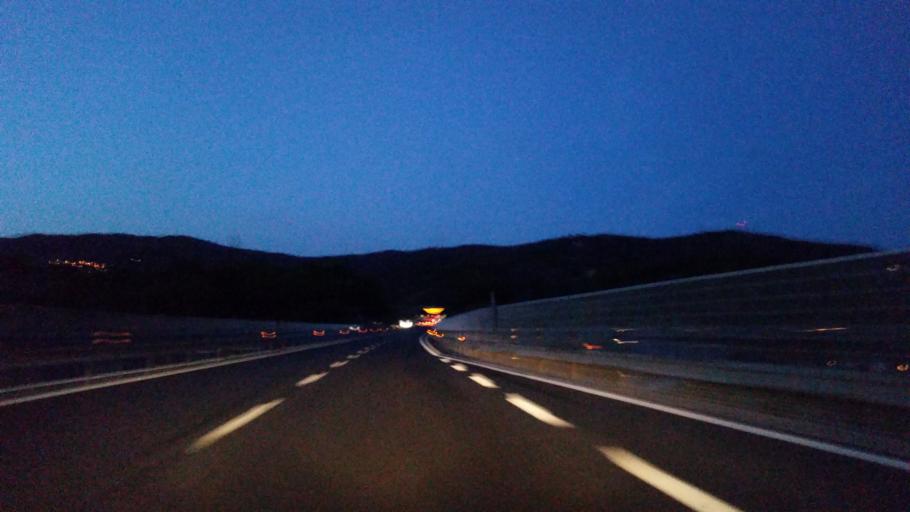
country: IT
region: Liguria
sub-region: Provincia di Imperia
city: San Bartolomeo al Mare
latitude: 43.9301
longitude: 8.0995
